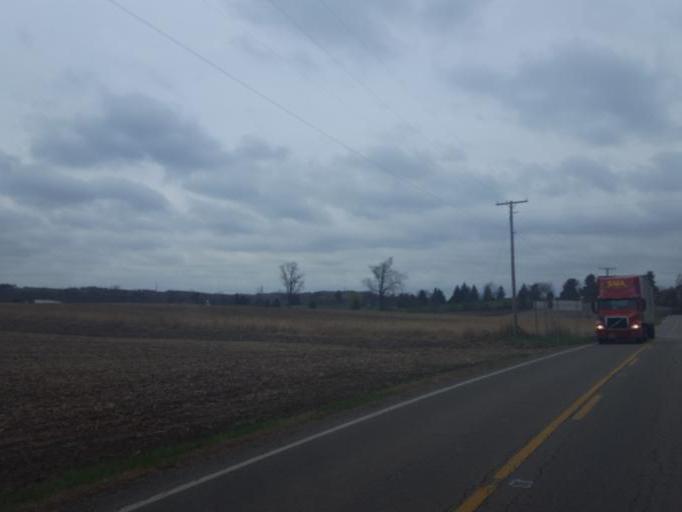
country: US
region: Ohio
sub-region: Ashland County
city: Loudonville
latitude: 40.6672
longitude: -82.1476
